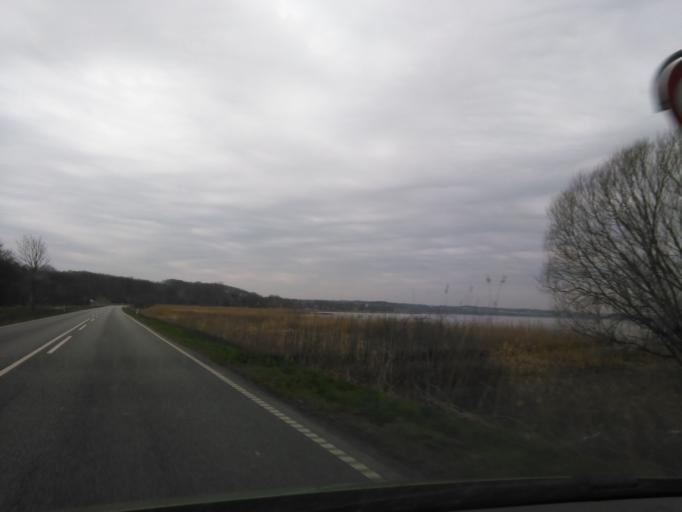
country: DK
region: North Denmark
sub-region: Mariagerfjord Kommune
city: Hadsund
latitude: 56.6992
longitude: 10.1134
